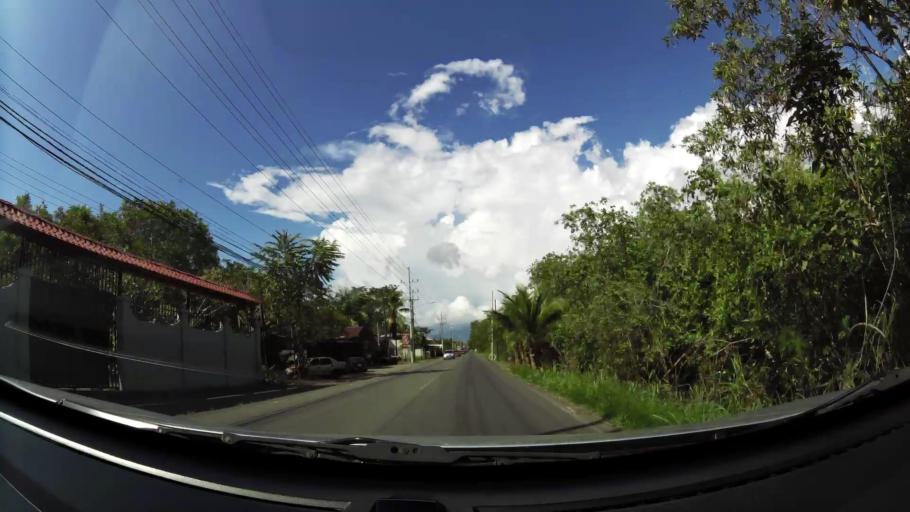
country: CR
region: Puntarenas
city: Quepos
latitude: 9.4407
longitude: -84.1649
